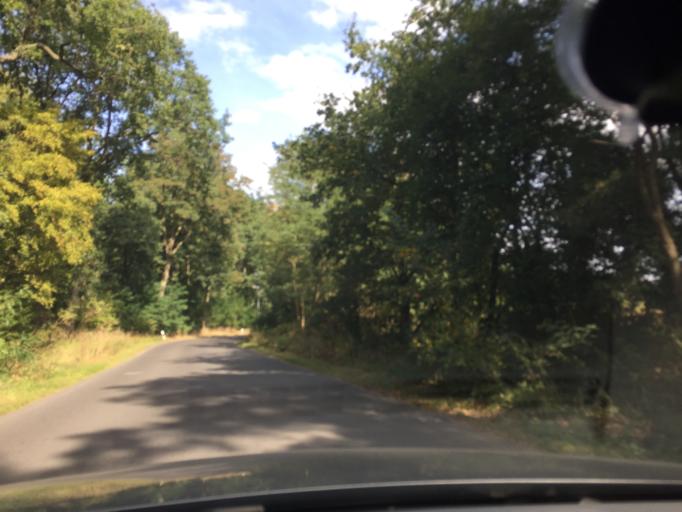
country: DE
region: Brandenburg
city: Spreenhagen
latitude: 52.3984
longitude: 13.9024
